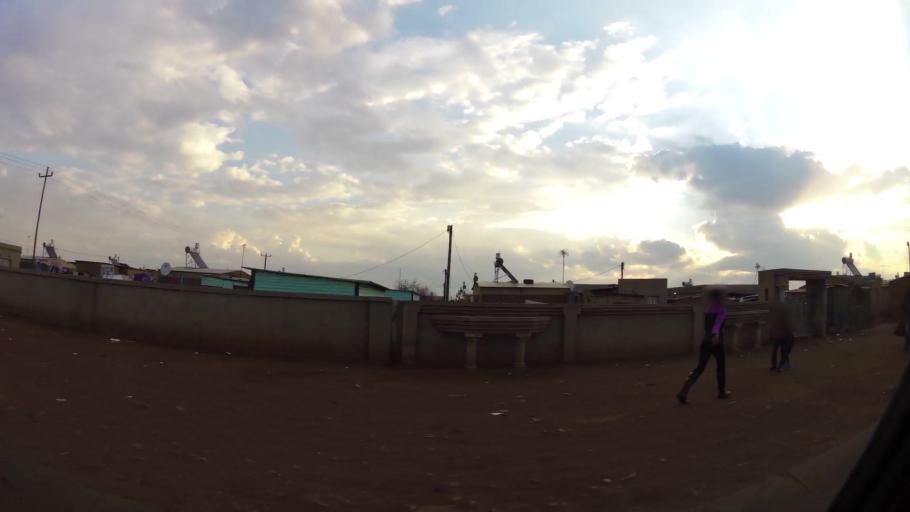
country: ZA
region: Gauteng
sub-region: City of Johannesburg Metropolitan Municipality
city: Orange Farm
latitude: -26.5626
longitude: 27.8333
